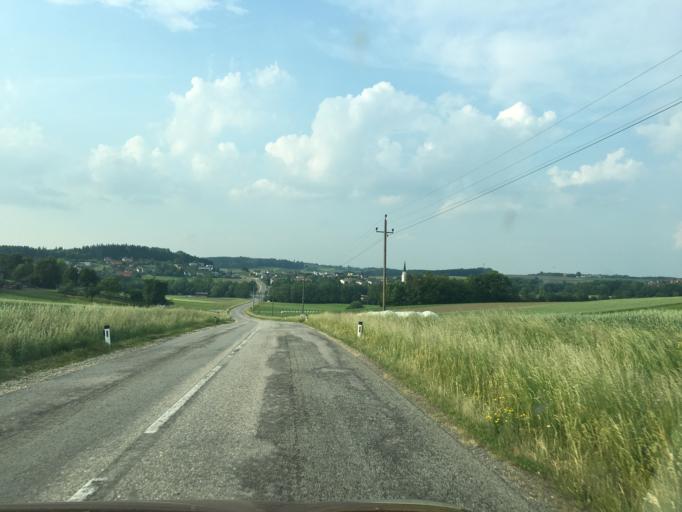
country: AT
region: Upper Austria
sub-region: Politischer Bezirk Ried im Innkreis
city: Ried im Innkreis
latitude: 48.1726
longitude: 13.5757
